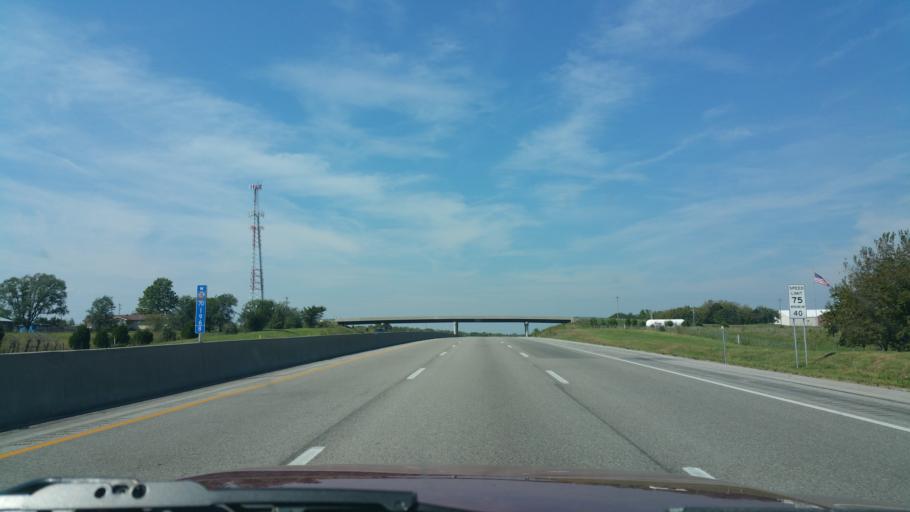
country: US
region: Kansas
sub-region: Douglas County
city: Lawrence
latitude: 38.9971
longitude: -95.3508
